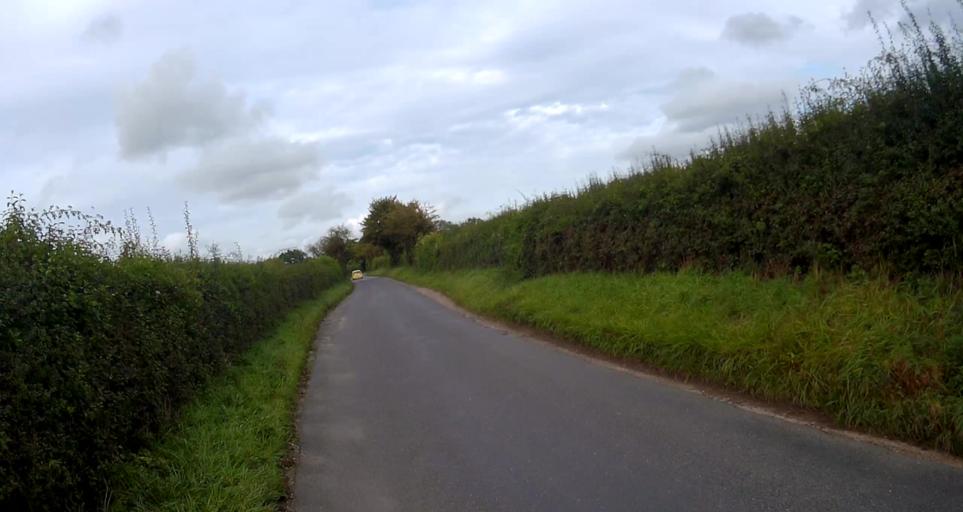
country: GB
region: England
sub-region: Hampshire
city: Four Marks
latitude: 51.1010
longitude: -1.1412
